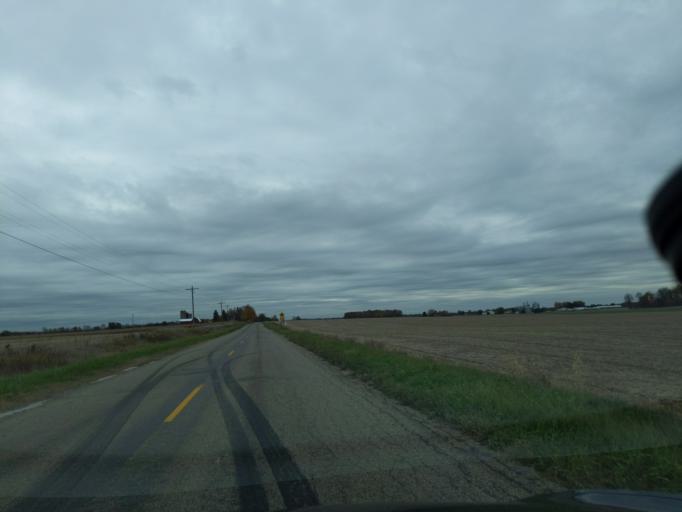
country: US
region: Michigan
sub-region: Eaton County
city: Eaton Rapids
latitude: 42.4463
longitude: -84.6006
